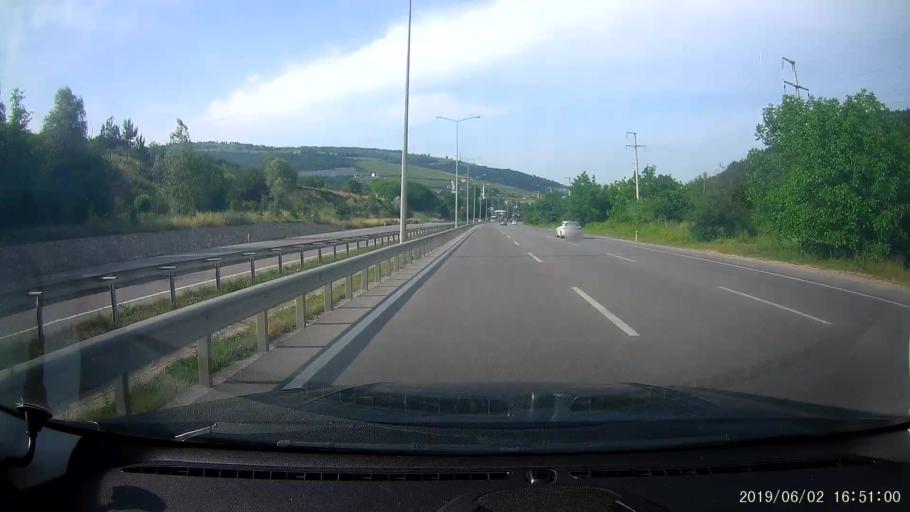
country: TR
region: Samsun
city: Taflan
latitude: 41.2664
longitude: 36.1772
